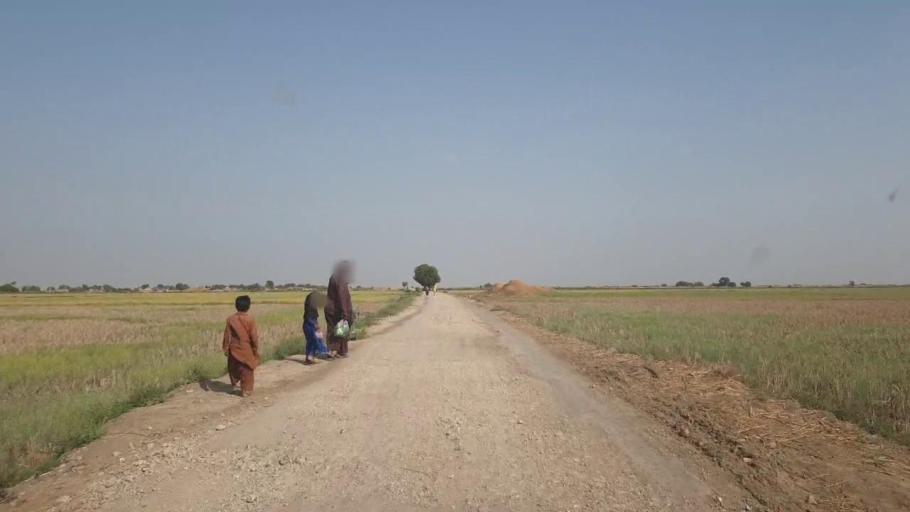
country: PK
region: Sindh
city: Kario
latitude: 24.5356
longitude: 68.5402
